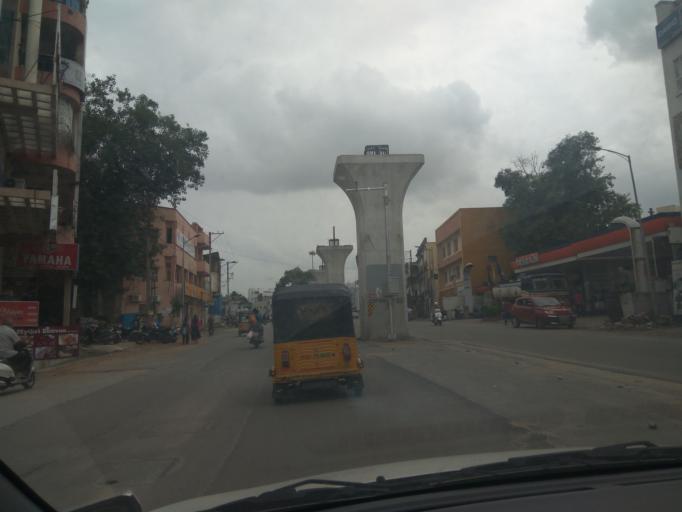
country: IN
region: Telangana
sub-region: Hyderabad
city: Hyderabad
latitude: 17.3964
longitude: 78.4914
